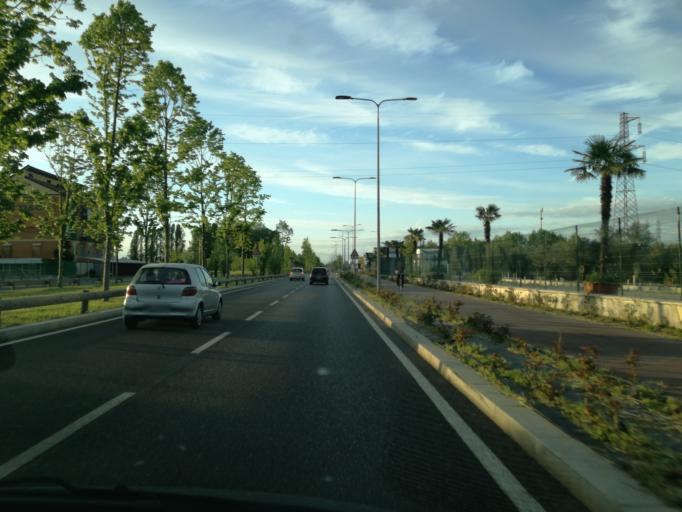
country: IT
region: Lombardy
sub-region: Citta metropolitana di Milano
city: Noverasco-Sporting Mirasole
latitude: 45.4059
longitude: 9.2084
